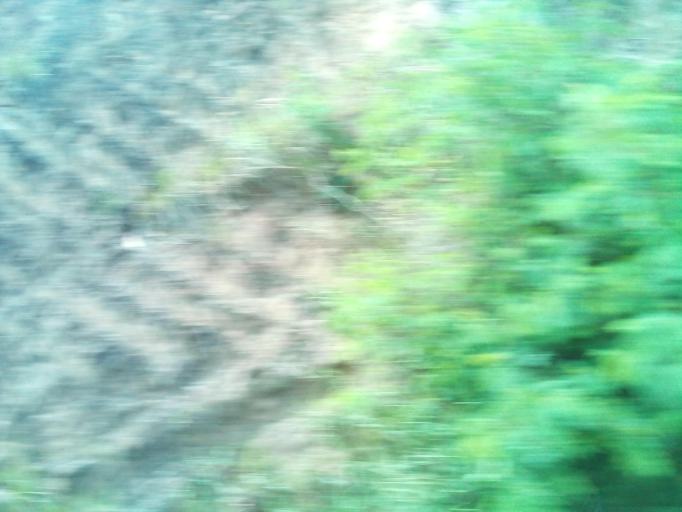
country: BR
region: Minas Gerais
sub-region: Caete
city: Caete
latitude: -19.8909
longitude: -43.7464
